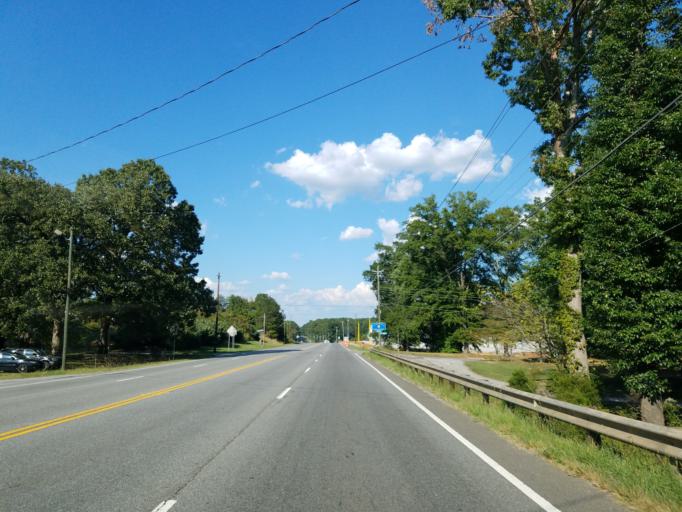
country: US
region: Georgia
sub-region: Bartow County
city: Cartersville
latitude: 34.2138
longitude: -84.7947
